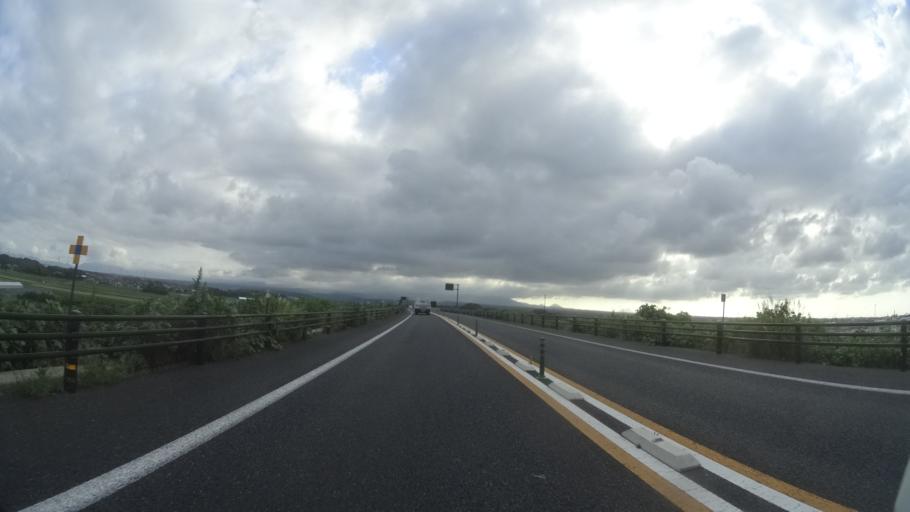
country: JP
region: Tottori
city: Kurayoshi
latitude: 35.4977
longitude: 133.7141
